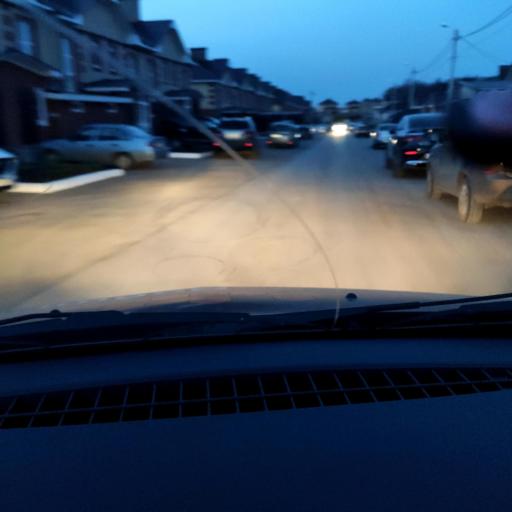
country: RU
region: Bashkortostan
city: Mikhaylovka
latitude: 54.8315
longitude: 55.8684
